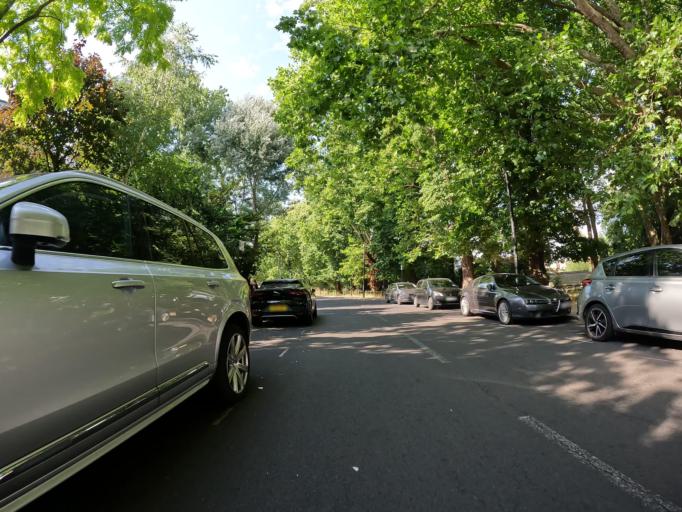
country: GB
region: England
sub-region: Greater London
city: Barnet
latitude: 51.6529
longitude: -0.1822
